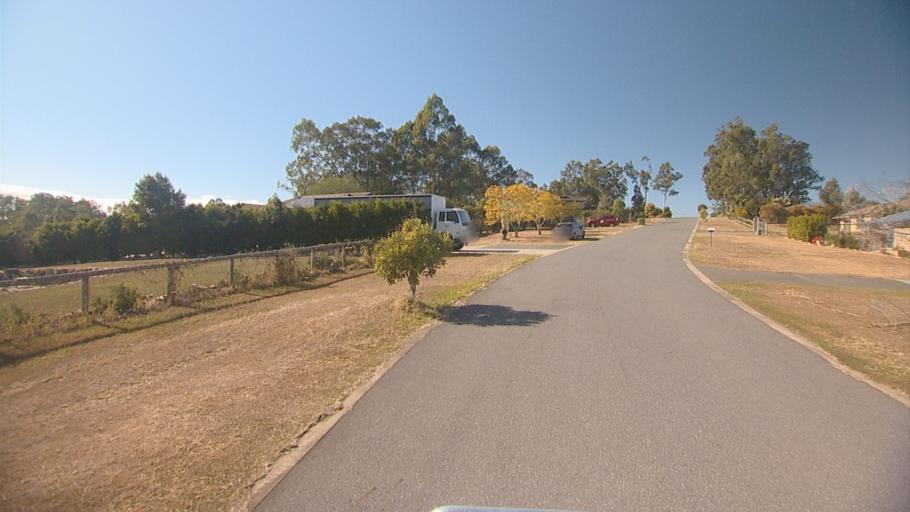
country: AU
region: Queensland
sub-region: Logan
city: Cedar Vale
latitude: -27.8664
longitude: 153.0015
